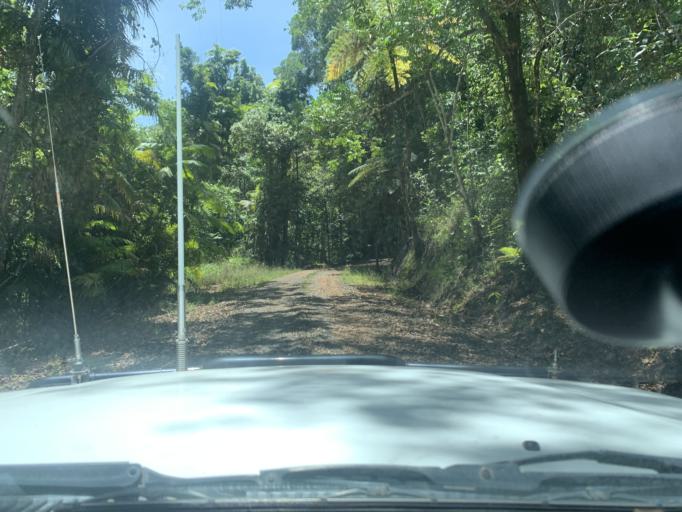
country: AU
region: Queensland
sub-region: Cairns
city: Woree
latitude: -16.9762
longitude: 145.6511
